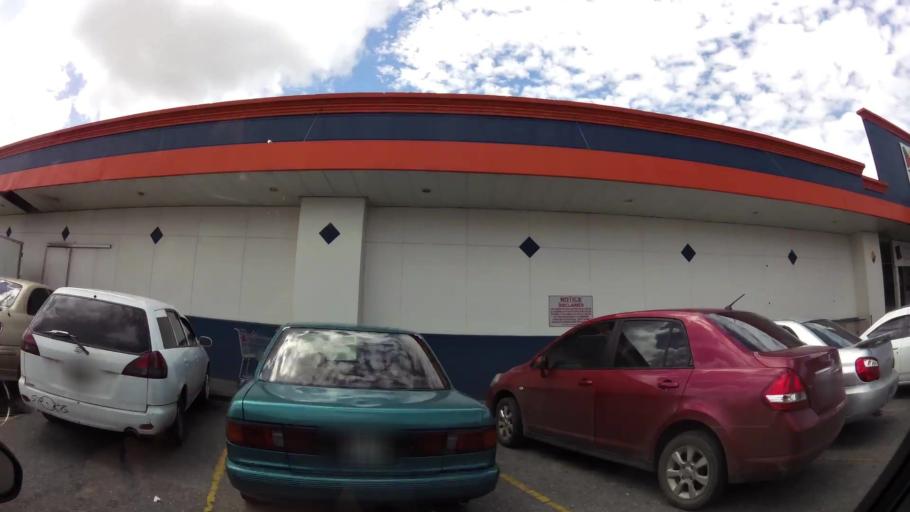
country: TT
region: City of San Fernando
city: Marabella
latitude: 10.3015
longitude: -61.4481
